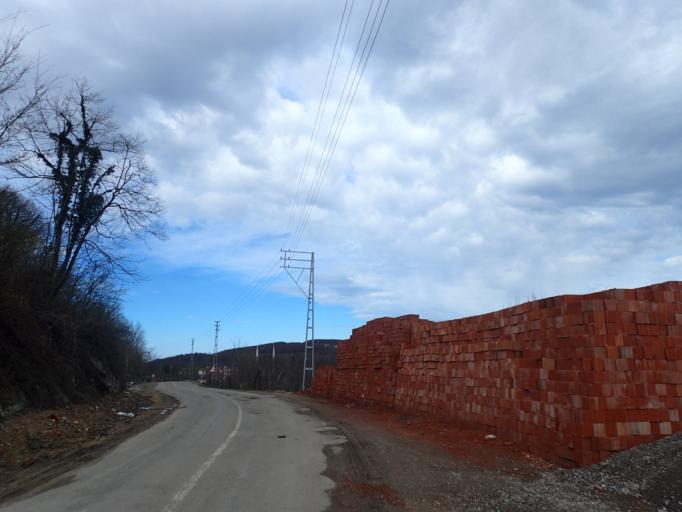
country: TR
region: Ordu
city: Kumru
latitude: 40.9375
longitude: 37.2612
